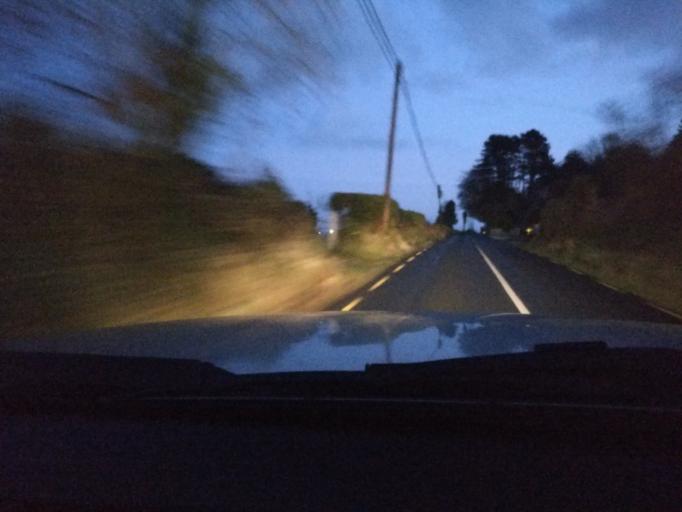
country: IE
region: Leinster
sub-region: Lu
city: Carlingford
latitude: 54.0580
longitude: -6.2012
